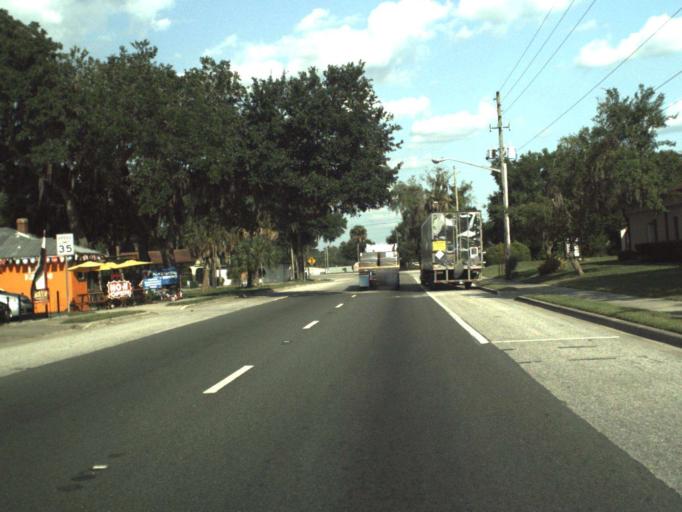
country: US
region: Florida
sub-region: Lake County
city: Groveland
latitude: 28.5595
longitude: -81.8557
